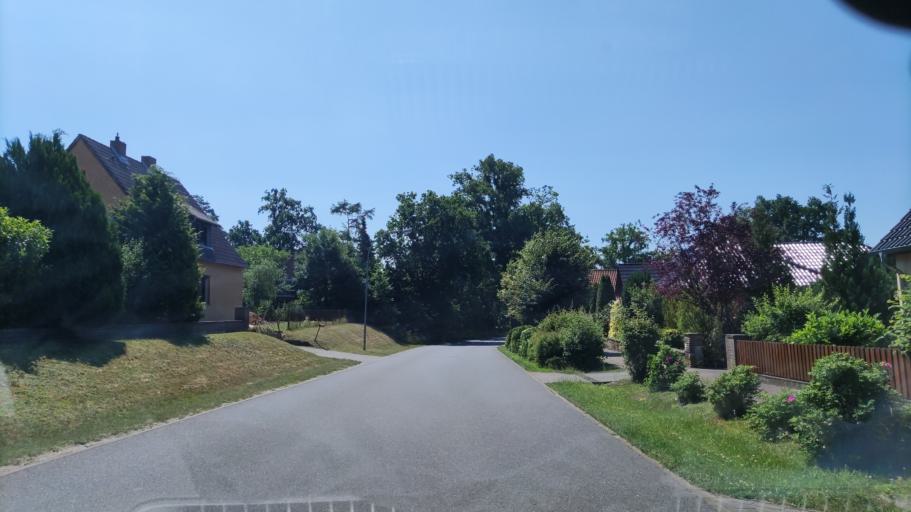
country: DE
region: Lower Saxony
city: Suderburg
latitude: 52.9195
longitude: 10.4613
